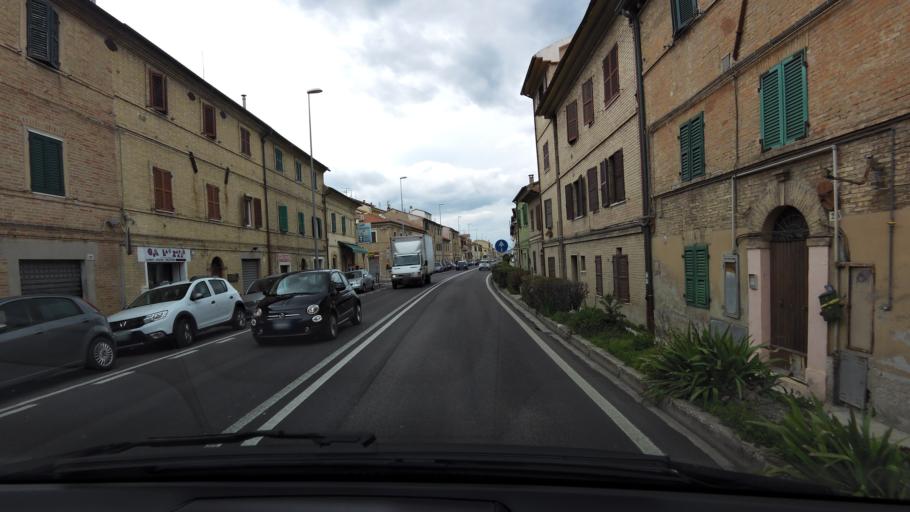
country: IT
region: The Marches
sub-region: Provincia di Ancona
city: Posatora
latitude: 43.6100
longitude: 13.4549
